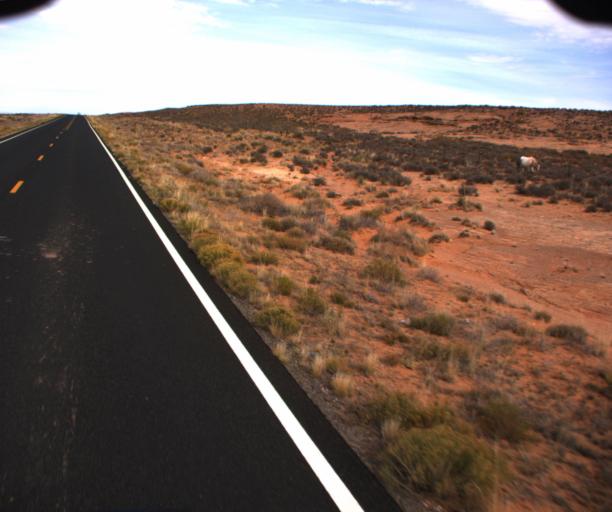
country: US
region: Arizona
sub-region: Apache County
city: Many Farms
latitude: 36.8790
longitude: -109.6297
